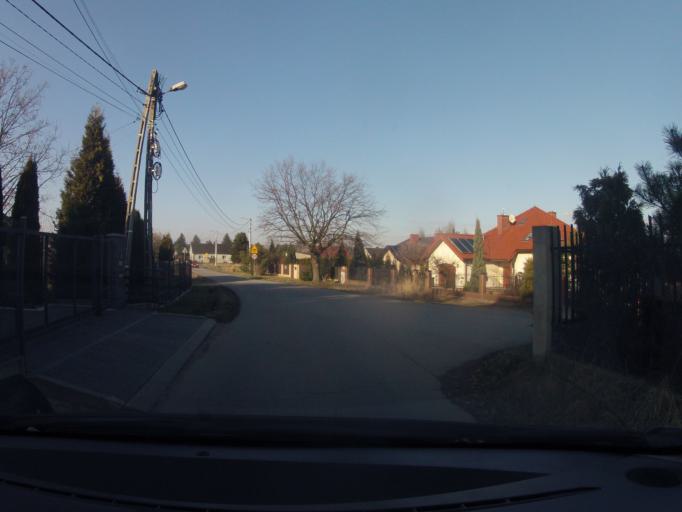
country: PL
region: Lesser Poland Voivodeship
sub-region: Powiat wielicki
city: Wieliczka
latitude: 49.9881
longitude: 20.0206
